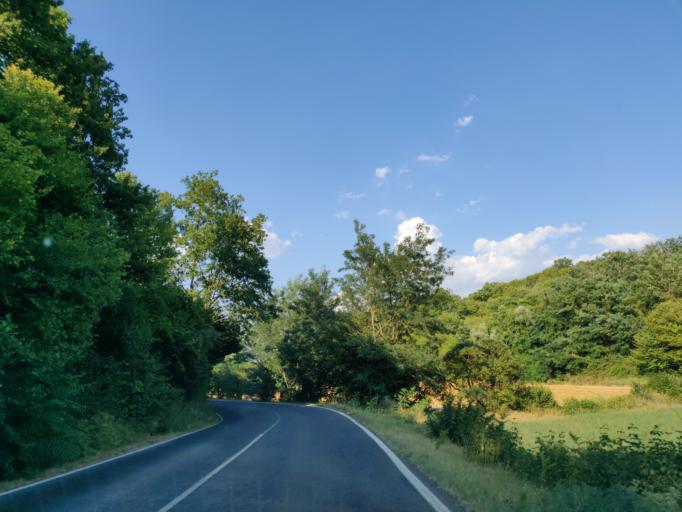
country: IT
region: Latium
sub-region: Provincia di Viterbo
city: Gradoli
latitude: 42.6502
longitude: 11.8424
